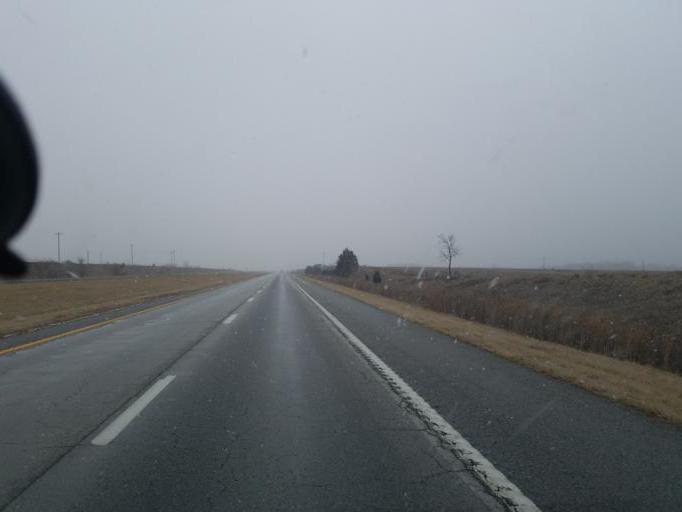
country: US
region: Missouri
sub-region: Macon County
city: La Plata
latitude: 39.9585
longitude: -92.4767
